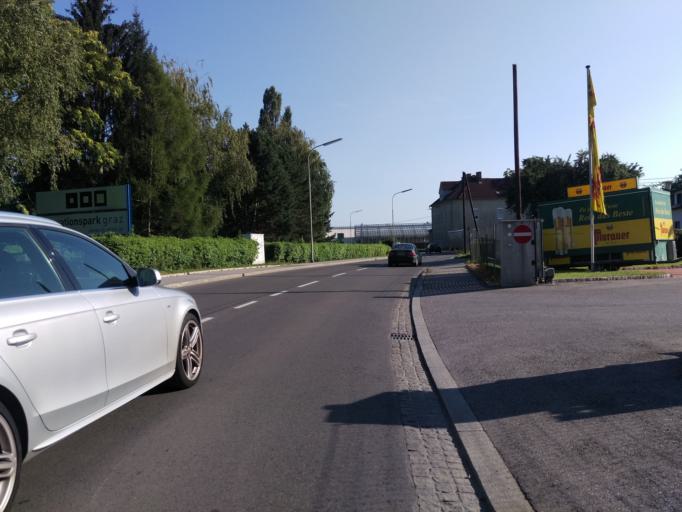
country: AT
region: Styria
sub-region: Graz Stadt
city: Graz
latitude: 47.0427
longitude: 15.4376
